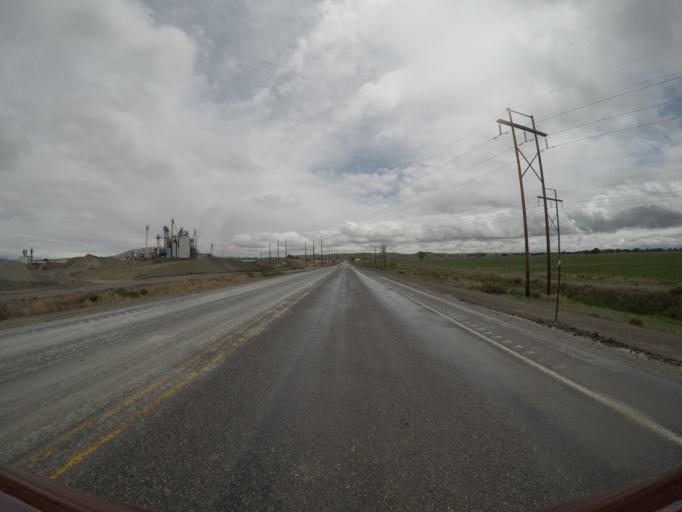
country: US
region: Wyoming
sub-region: Big Horn County
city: Lovell
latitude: 44.8570
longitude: -108.3316
